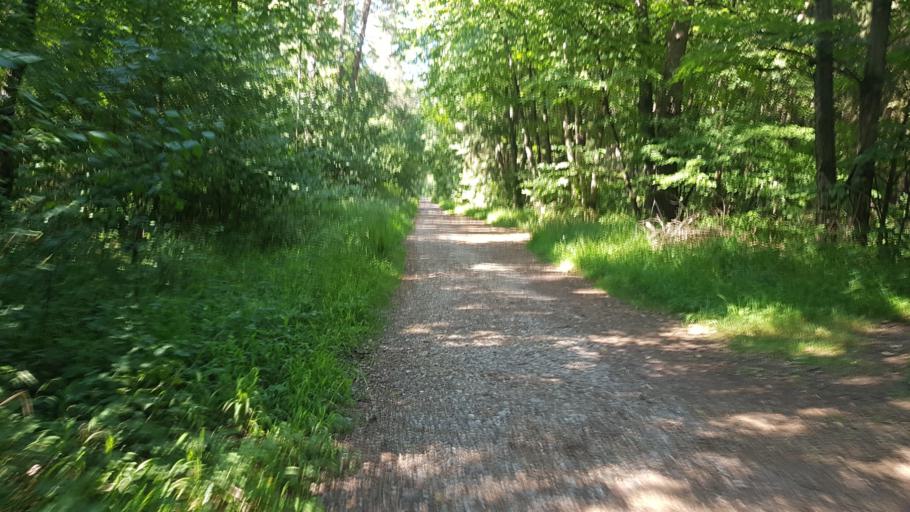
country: DE
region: Bavaria
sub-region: Upper Bavaria
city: Oberschleissheim
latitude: 48.2202
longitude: 11.5691
